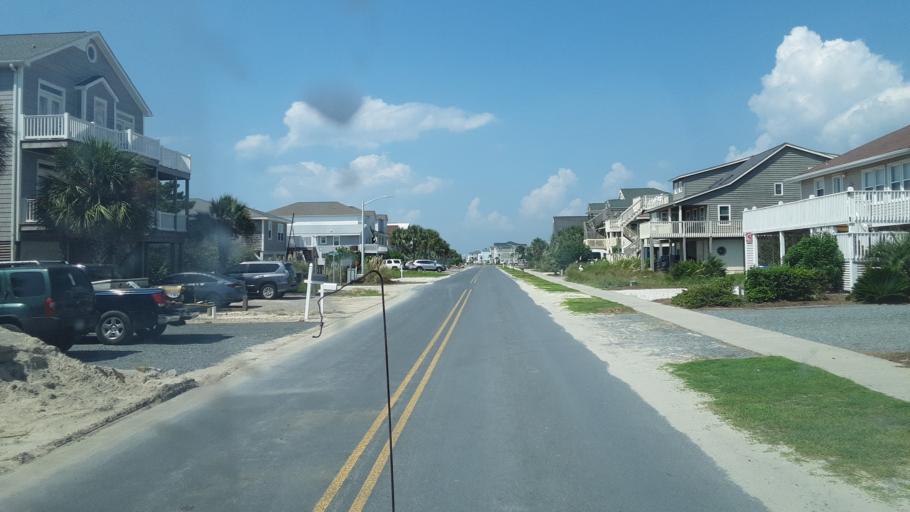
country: US
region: North Carolina
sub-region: Brunswick County
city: Shallotte
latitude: 33.8969
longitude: -78.3992
